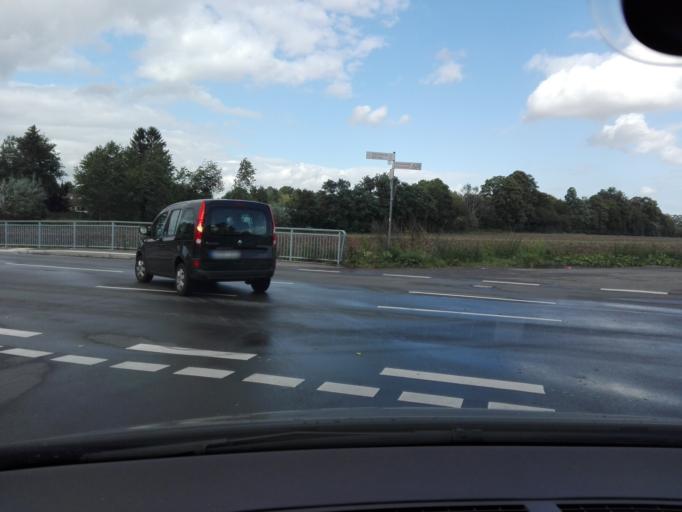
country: DE
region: North Rhine-Westphalia
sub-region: Regierungsbezirk Arnsberg
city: Unna
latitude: 51.5307
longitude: 7.7007
